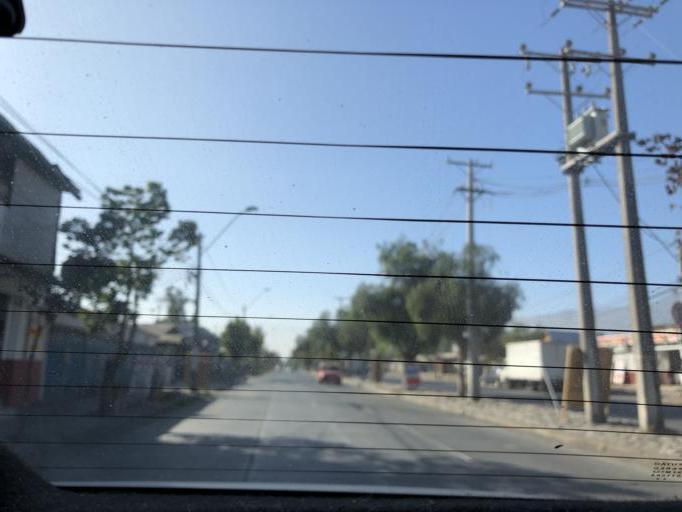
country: CL
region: Santiago Metropolitan
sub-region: Provincia de Cordillera
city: Puente Alto
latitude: -33.6188
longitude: -70.5928
